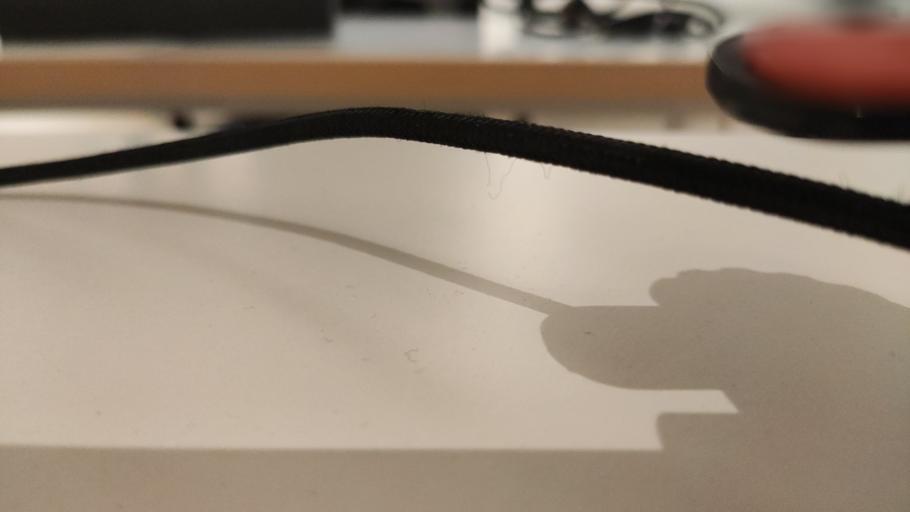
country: RU
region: Moskovskaya
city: Dorokhovo
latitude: 55.3997
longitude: 36.3826
